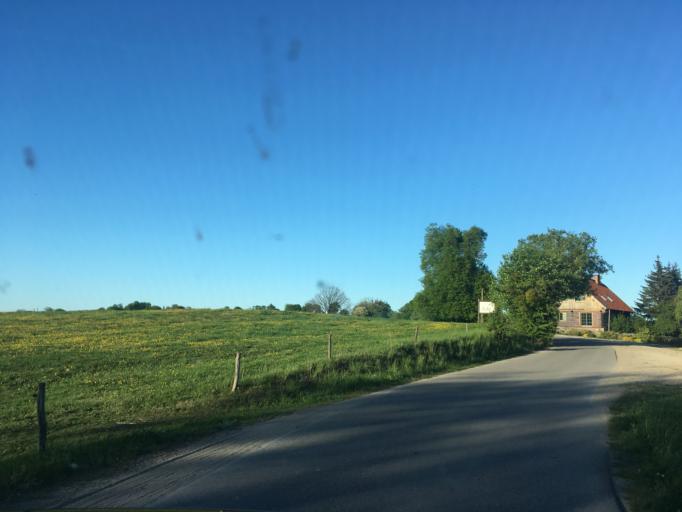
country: PL
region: Warmian-Masurian Voivodeship
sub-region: Powiat piski
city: Ruciane-Nida
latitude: 53.6882
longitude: 21.4739
